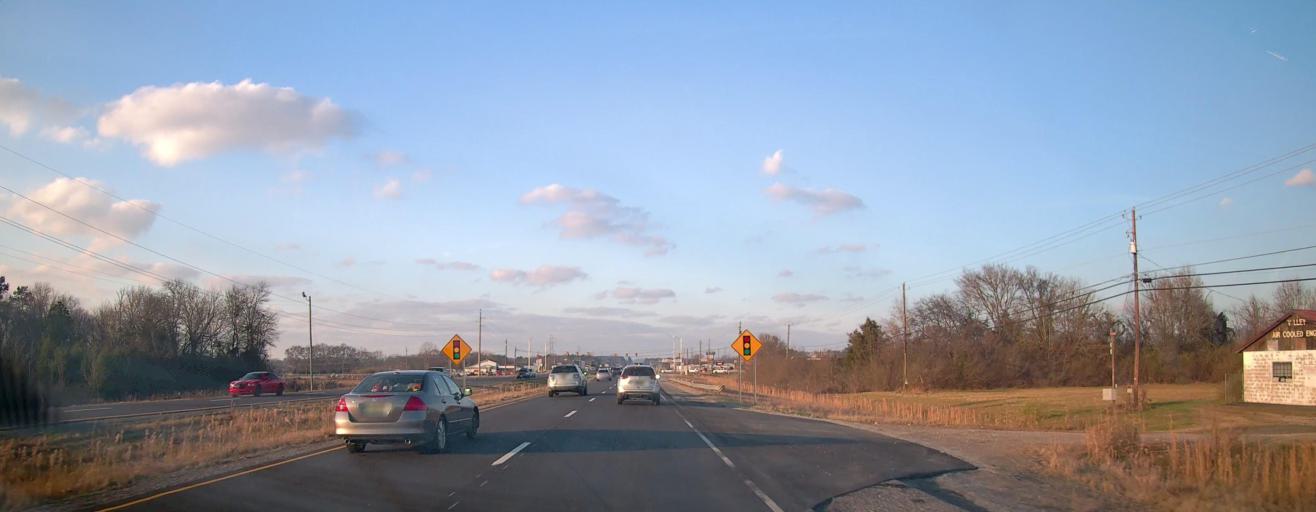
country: US
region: Alabama
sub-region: Calhoun County
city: Alexandria
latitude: 33.7655
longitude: -85.8919
